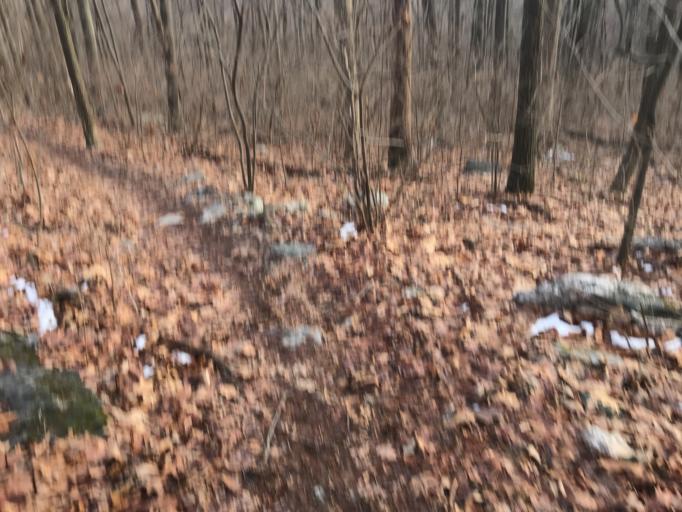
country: US
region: Maryland
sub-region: Frederick County
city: Braddock Heights
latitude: 39.4604
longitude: -77.4962
